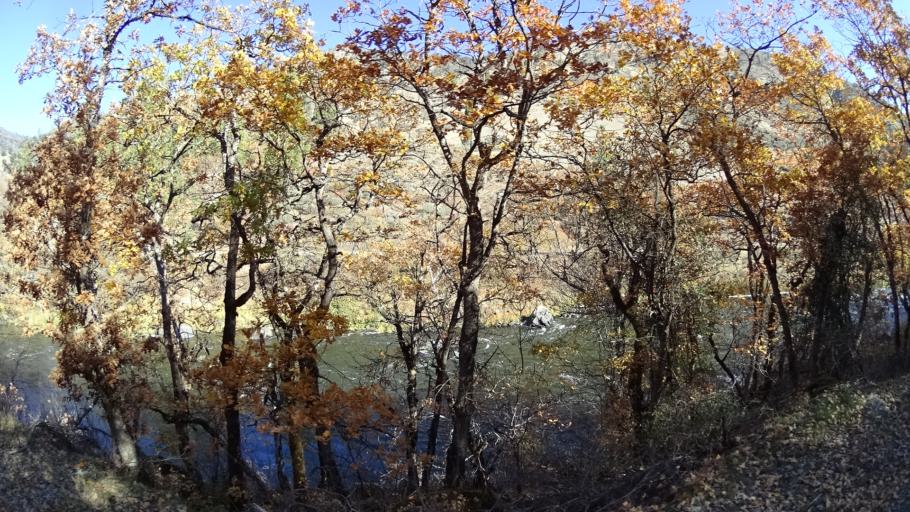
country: US
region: California
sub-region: Siskiyou County
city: Yreka
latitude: 41.8614
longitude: -122.7831
